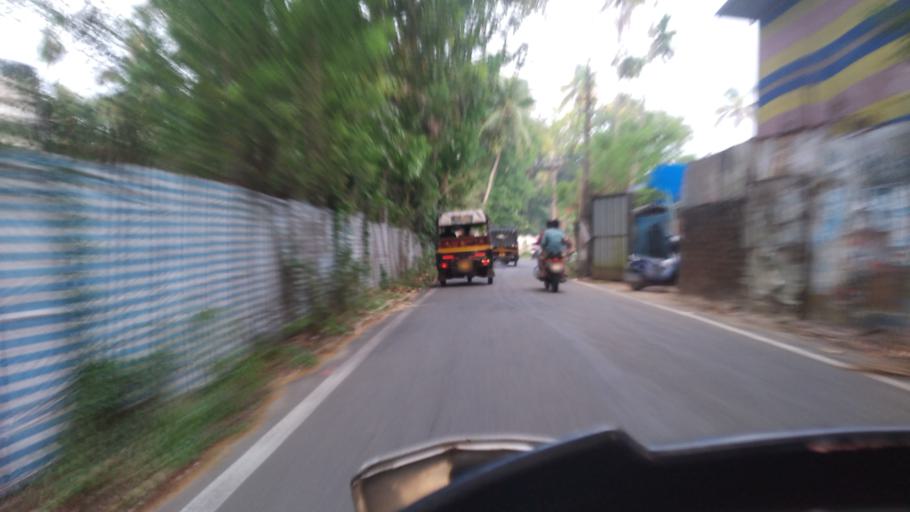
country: IN
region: Kerala
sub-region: Thrissur District
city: Kodungallur
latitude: 10.1639
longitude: 76.2082
